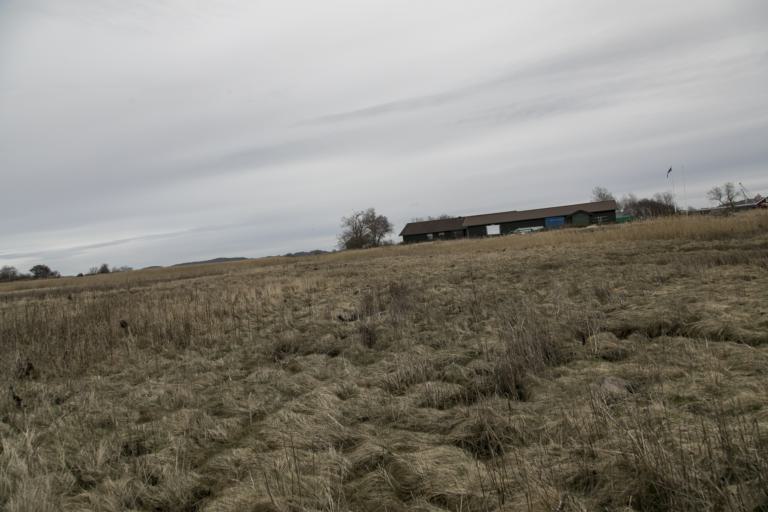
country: SE
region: Halland
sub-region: Varbergs Kommun
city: Varberg
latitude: 57.1196
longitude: 12.2282
